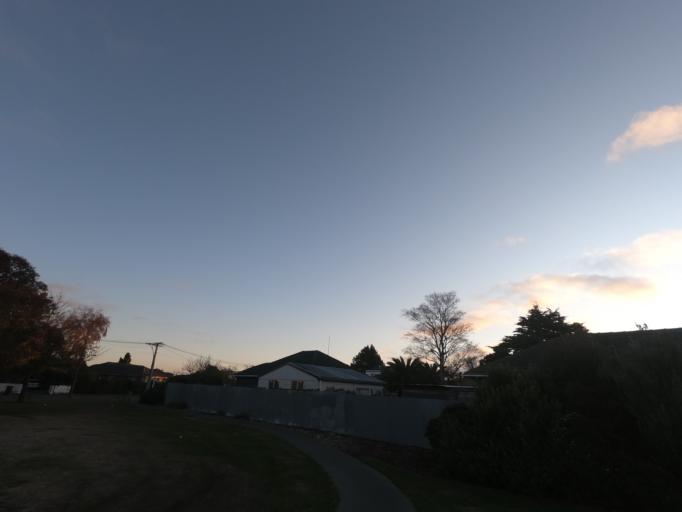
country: NZ
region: Canterbury
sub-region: Selwyn District
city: Prebbleton
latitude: -43.5750
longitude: 172.5623
